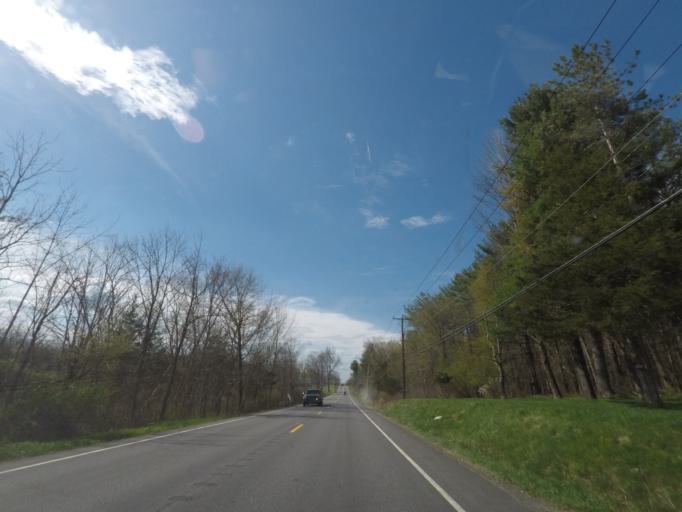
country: US
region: New York
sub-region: Greene County
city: Cairo
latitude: 42.3380
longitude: -74.0247
